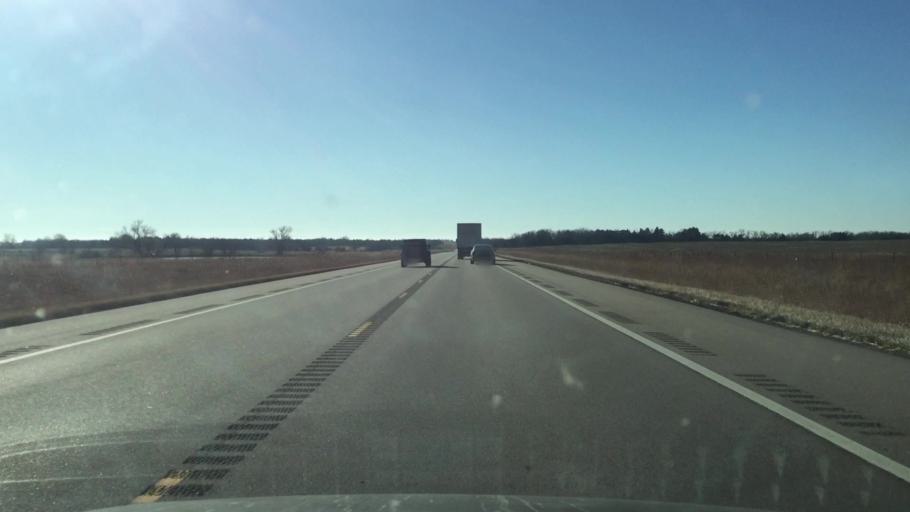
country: US
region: Kansas
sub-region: Allen County
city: Iola
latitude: 38.0456
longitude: -95.3805
